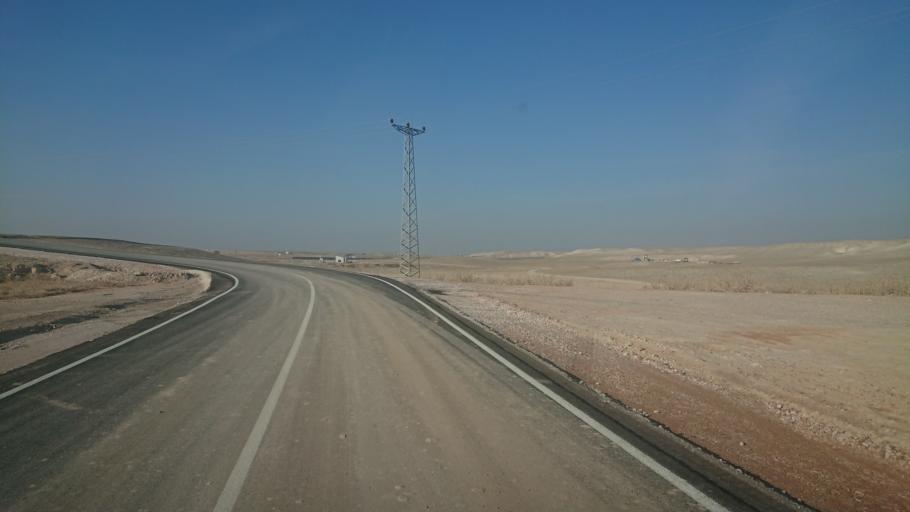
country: TR
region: Aksaray
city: Sultanhani
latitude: 38.0885
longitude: 33.6152
